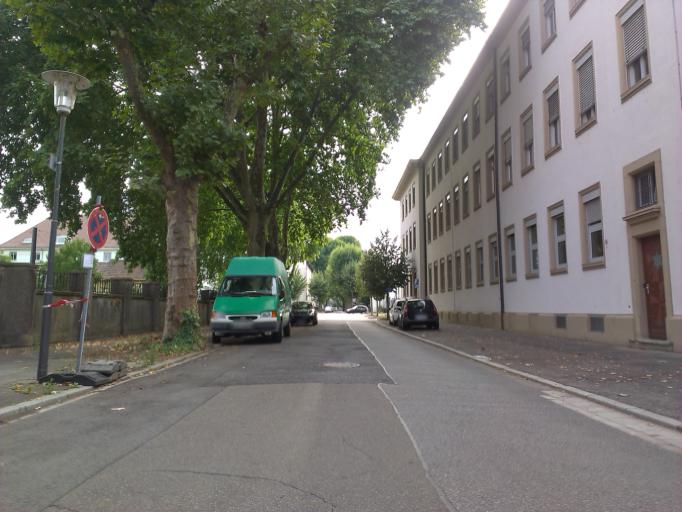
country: DE
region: Rheinland-Pfalz
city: Ludwigshafen am Rhein
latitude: 49.4721
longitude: 8.4528
